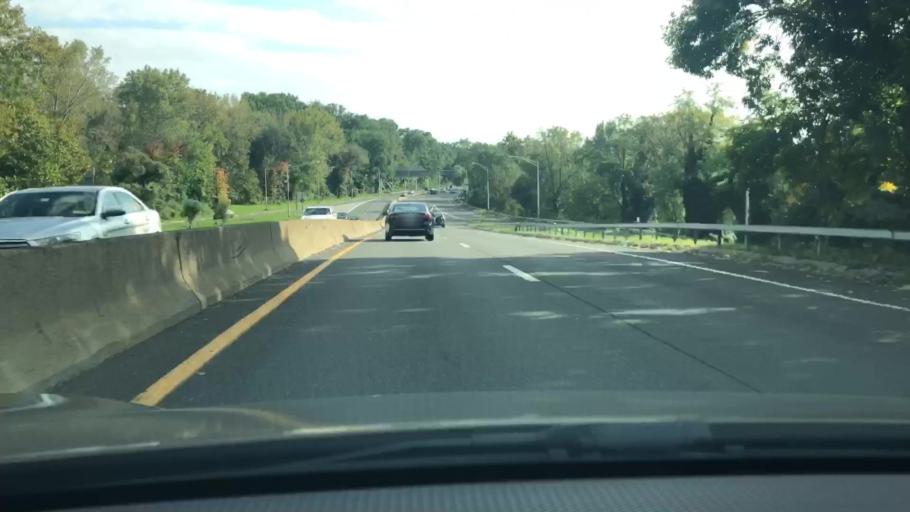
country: US
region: New York
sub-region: Westchester County
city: Pelham Manor
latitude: 40.8914
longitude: -73.8158
